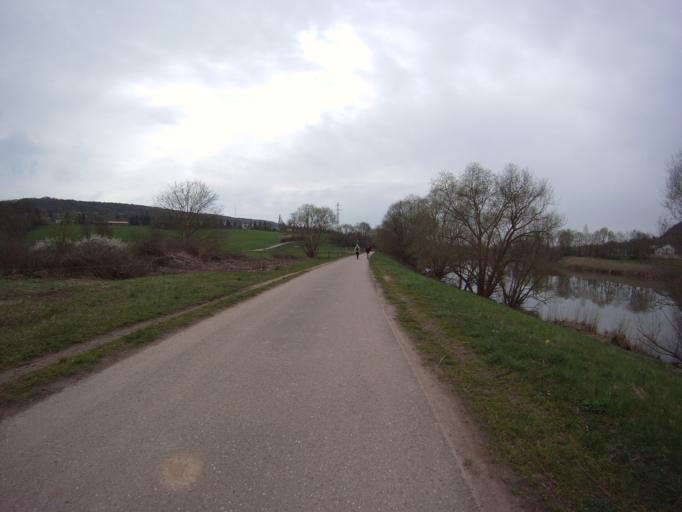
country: FR
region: Lorraine
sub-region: Departement de Meurthe-et-Moselle
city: Champigneulles
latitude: 48.7319
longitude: 6.1742
